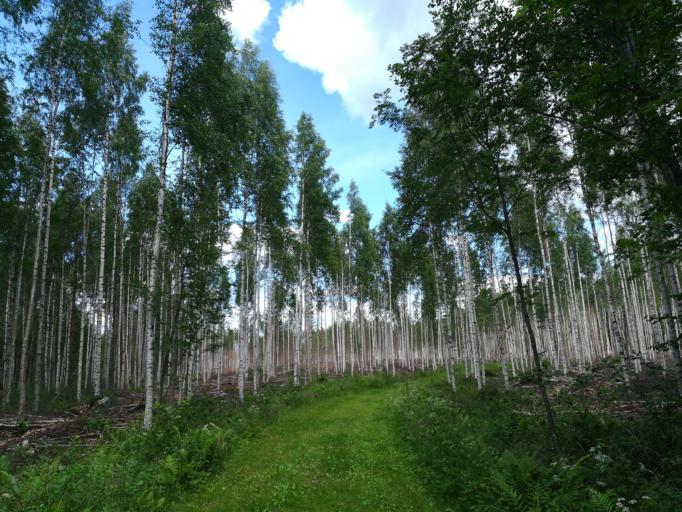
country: FI
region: Southern Savonia
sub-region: Mikkeli
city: Hirvensalmi
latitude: 61.6527
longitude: 26.7806
